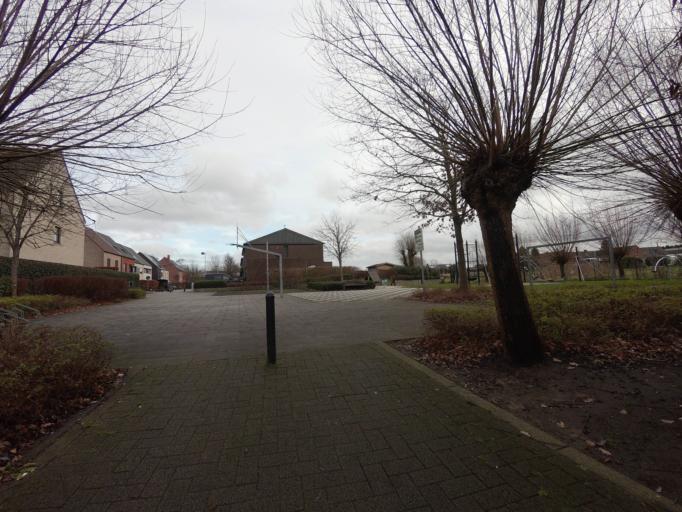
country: BE
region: Flanders
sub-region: Provincie Antwerpen
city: Duffel
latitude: 51.0875
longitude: 4.5135
